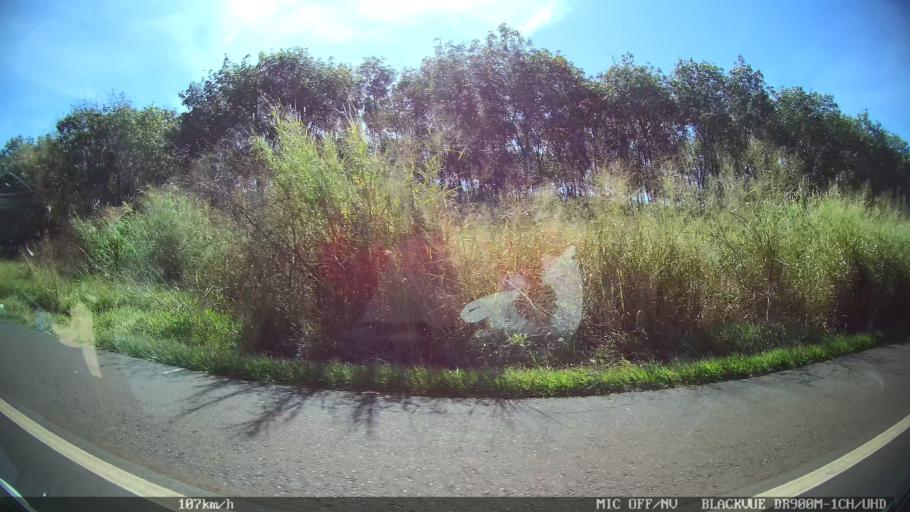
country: BR
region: Sao Paulo
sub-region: Franca
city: Franca
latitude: -20.5586
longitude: -47.5445
